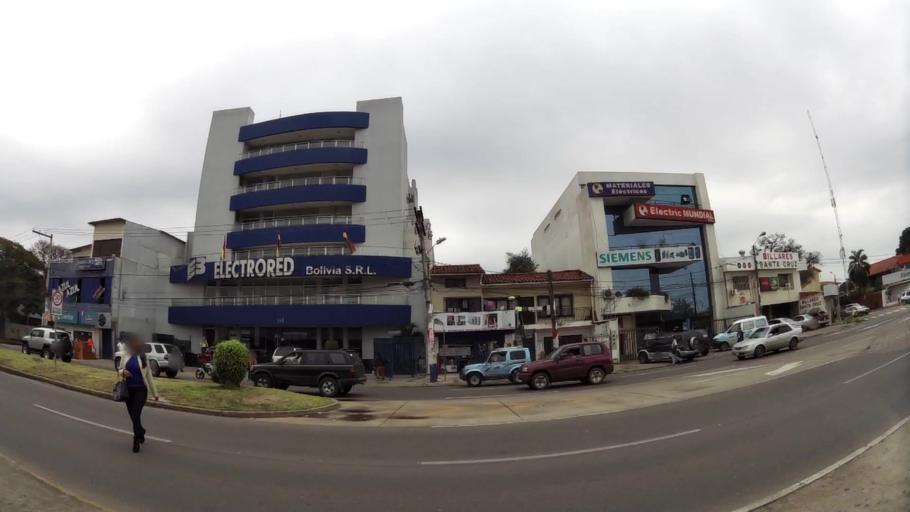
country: BO
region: Santa Cruz
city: Santa Cruz de la Sierra
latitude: -17.7787
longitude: -63.1649
